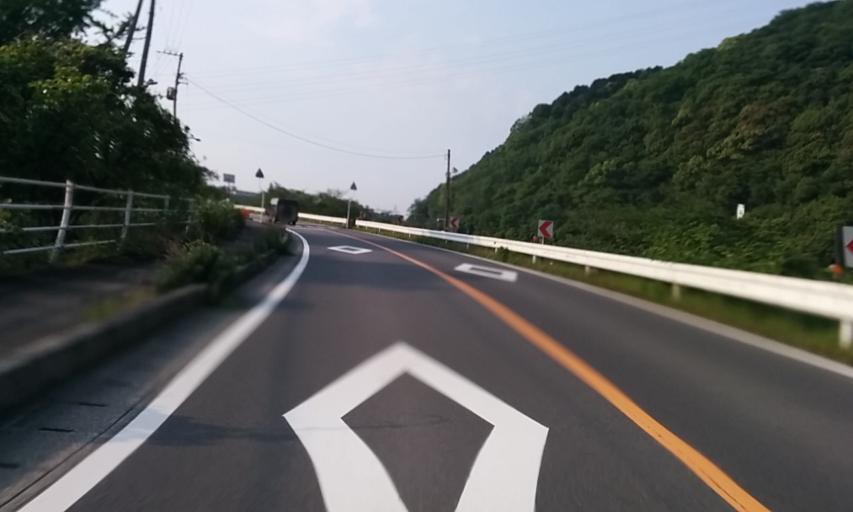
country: JP
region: Ehime
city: Saijo
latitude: 33.8943
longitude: 133.1944
